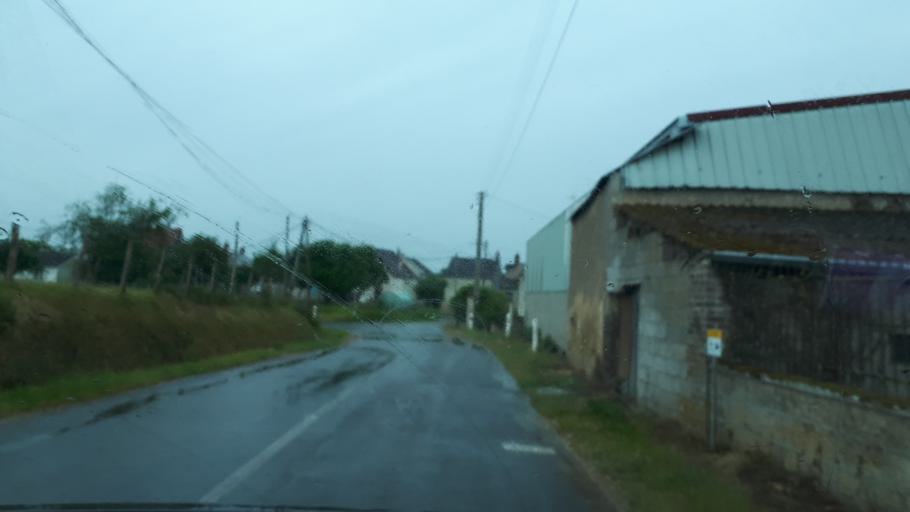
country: FR
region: Centre
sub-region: Departement du Loir-et-Cher
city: Lunay
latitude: 47.7940
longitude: 0.8999
